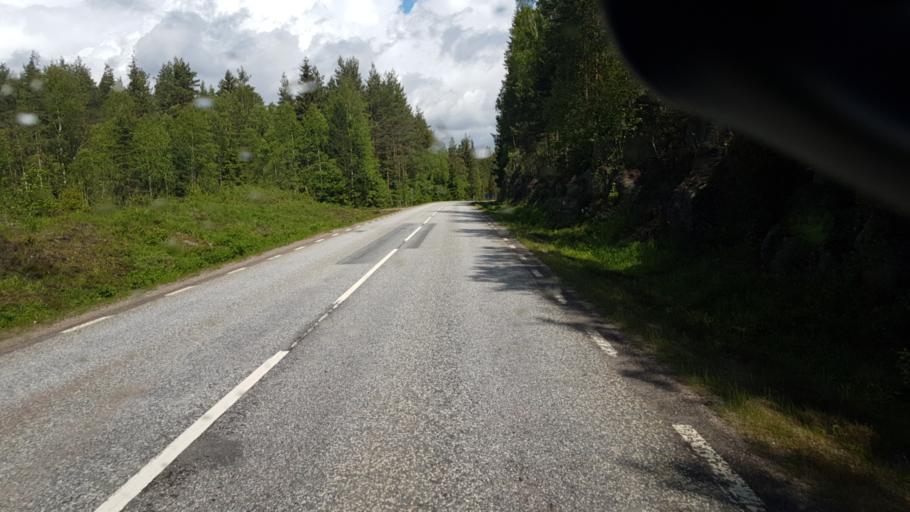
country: SE
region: Vaermland
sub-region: Eda Kommun
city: Amotfors
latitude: 59.5907
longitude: 12.2969
